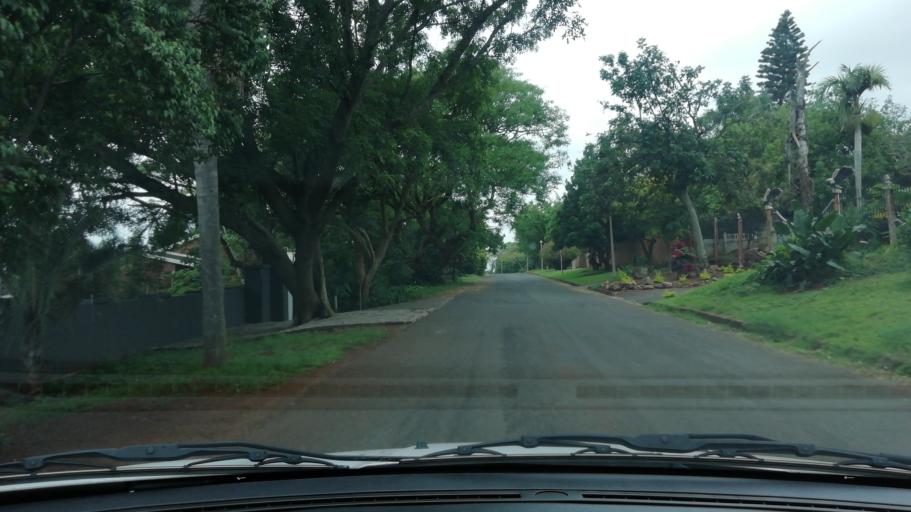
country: ZA
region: KwaZulu-Natal
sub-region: uThungulu District Municipality
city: Empangeni
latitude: -28.7550
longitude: 31.8875
